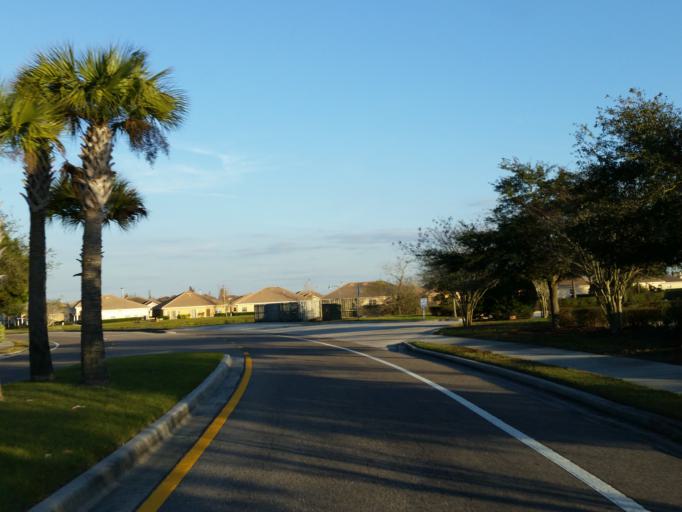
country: US
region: Florida
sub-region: Hillsborough County
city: Progress Village
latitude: 27.9205
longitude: -82.3264
